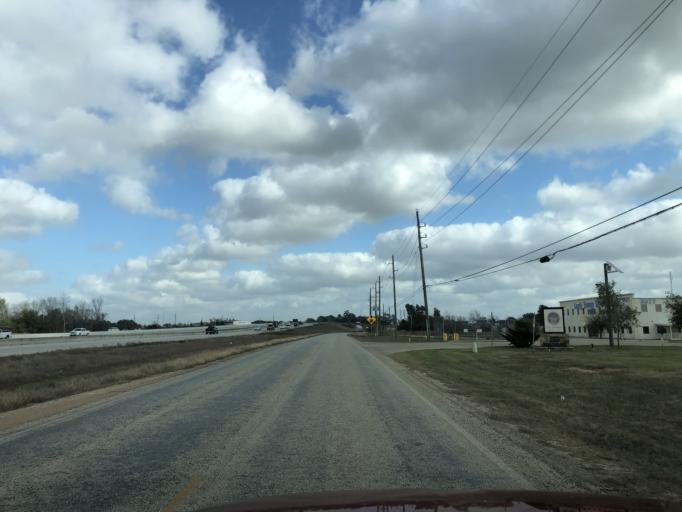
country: US
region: Texas
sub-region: Austin County
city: Sealy
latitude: 29.7705
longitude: -96.1371
